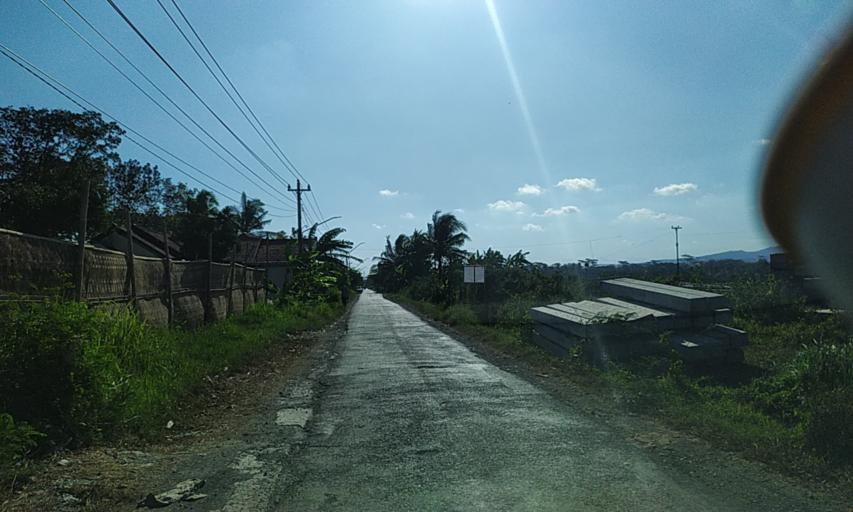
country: ID
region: Central Java
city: Krikil
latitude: -7.6190
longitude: 109.1355
